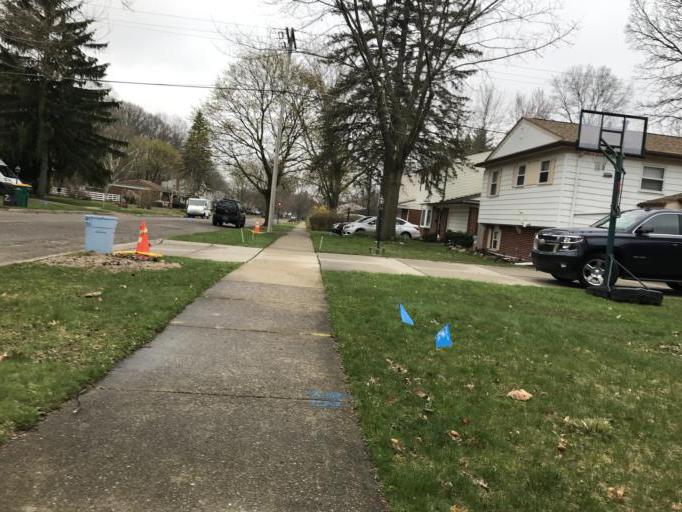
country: US
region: Michigan
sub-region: Oakland County
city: Farmington
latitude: 42.4672
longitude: -83.3431
